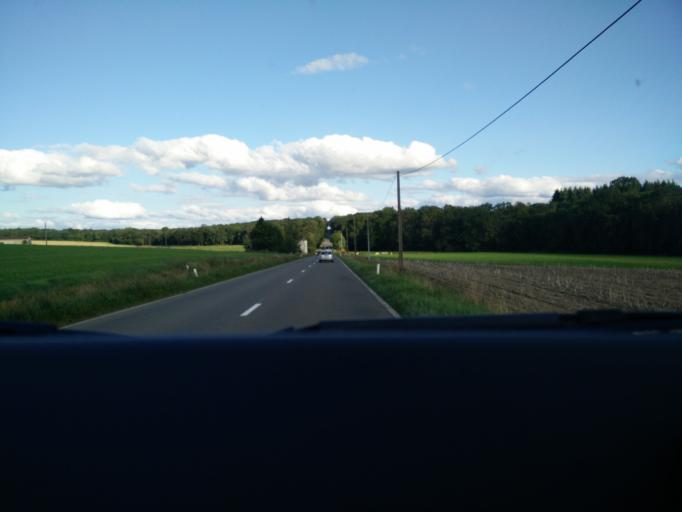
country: BE
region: Wallonia
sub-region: Province de Namur
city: Walcourt
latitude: 50.2078
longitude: 4.4734
